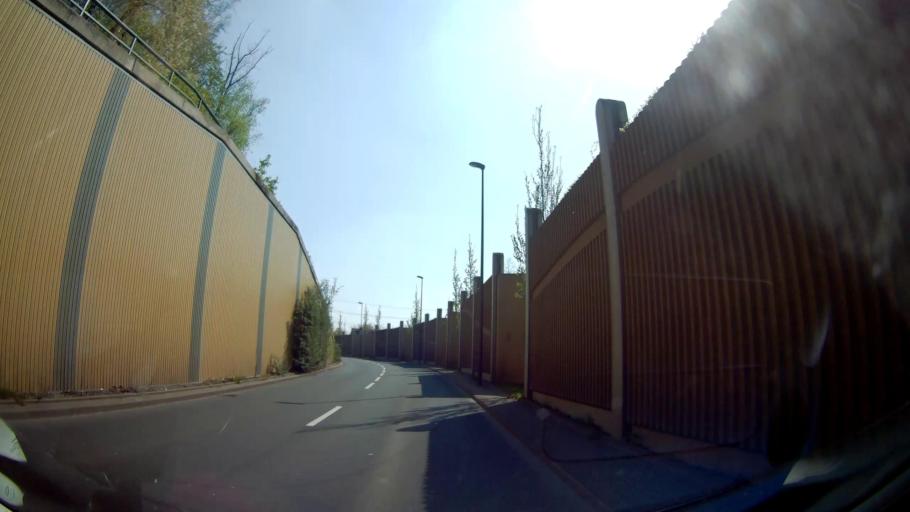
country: DE
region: North Rhine-Westphalia
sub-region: Regierungsbezirk Munster
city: Gelsenkirchen
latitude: 51.5041
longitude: 7.1372
